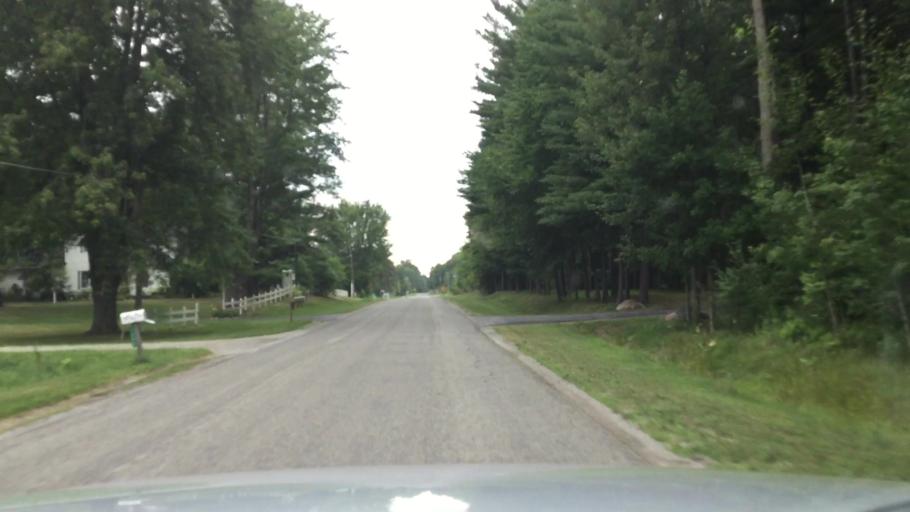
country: US
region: Michigan
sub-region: Saginaw County
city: Birch Run
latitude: 43.3071
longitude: -83.8072
